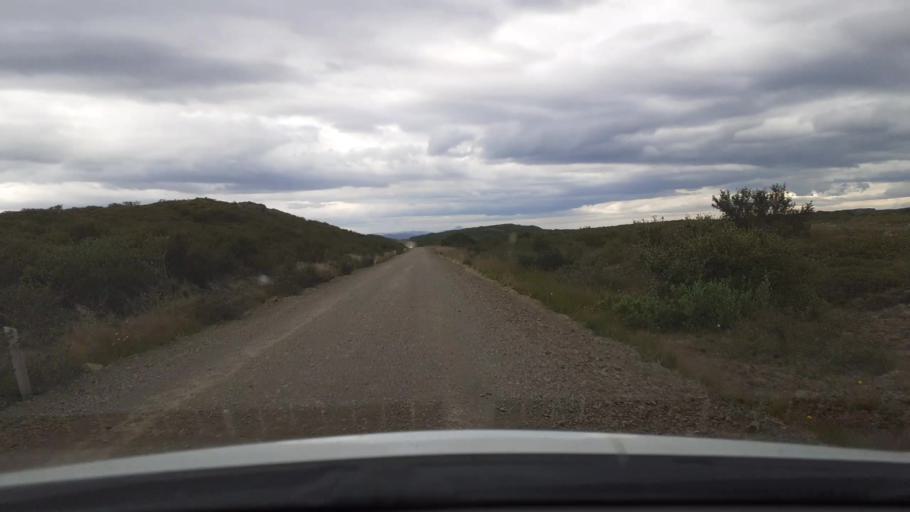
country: IS
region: West
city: Borgarnes
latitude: 64.5955
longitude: -21.9836
